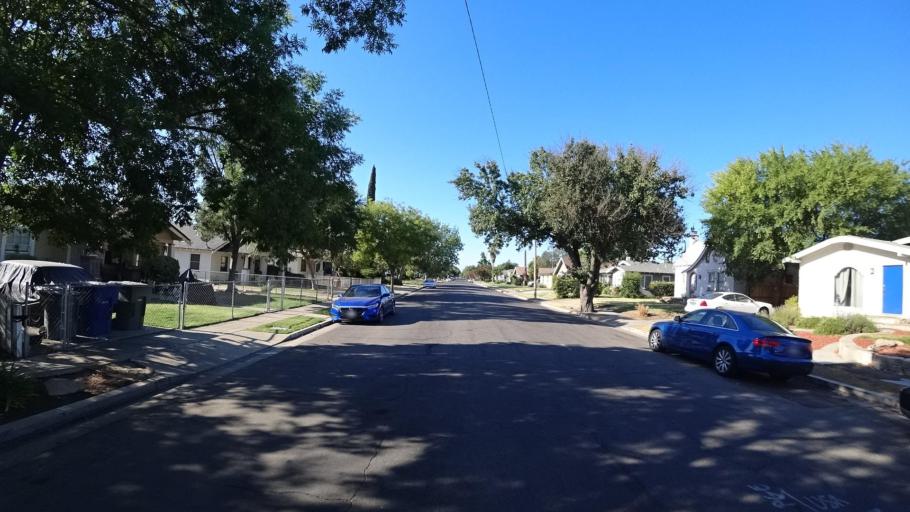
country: US
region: California
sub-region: Fresno County
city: Fresno
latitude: 36.7610
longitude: -119.8120
